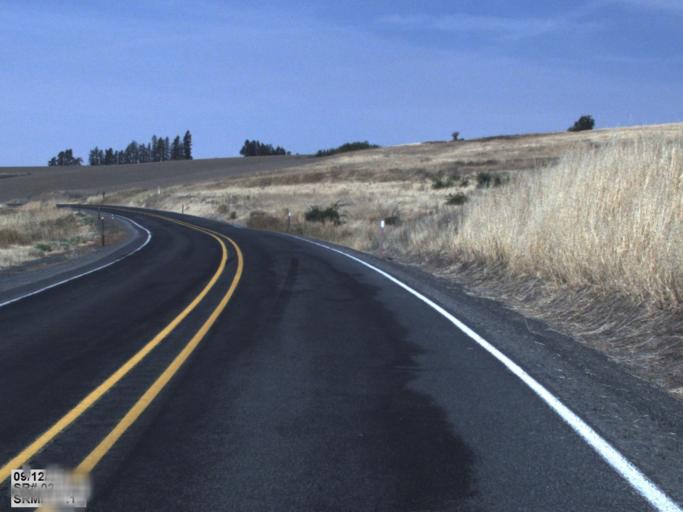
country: US
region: Idaho
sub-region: Benewah County
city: Plummer
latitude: 47.2393
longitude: -117.1201
